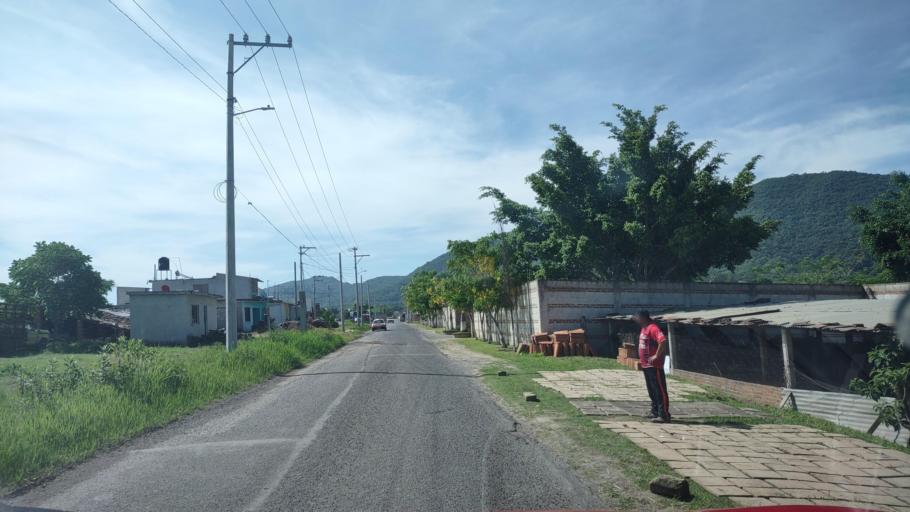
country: MX
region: Veracruz
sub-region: Emiliano Zapata
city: Dos Rios
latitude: 19.4307
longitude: -96.8013
